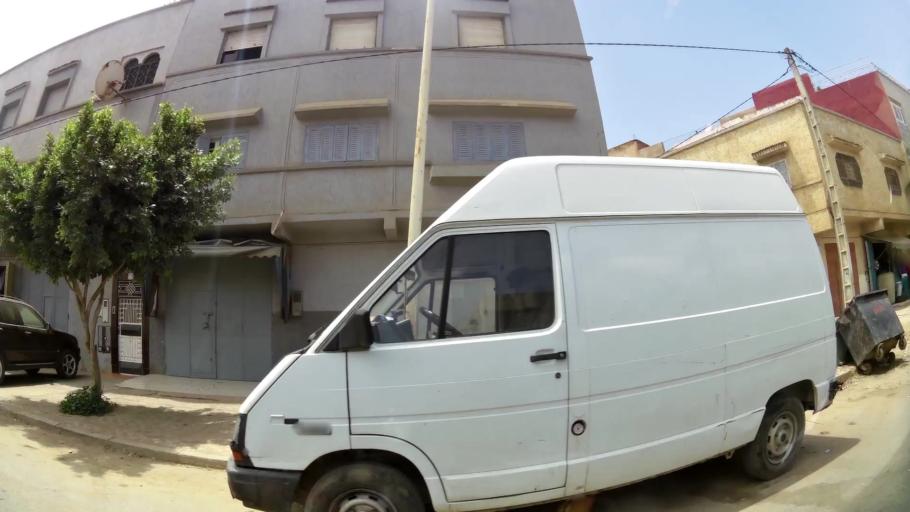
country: MA
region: Rabat-Sale-Zemmour-Zaer
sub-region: Khemisset
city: Khemisset
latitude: 33.8233
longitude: -6.0771
